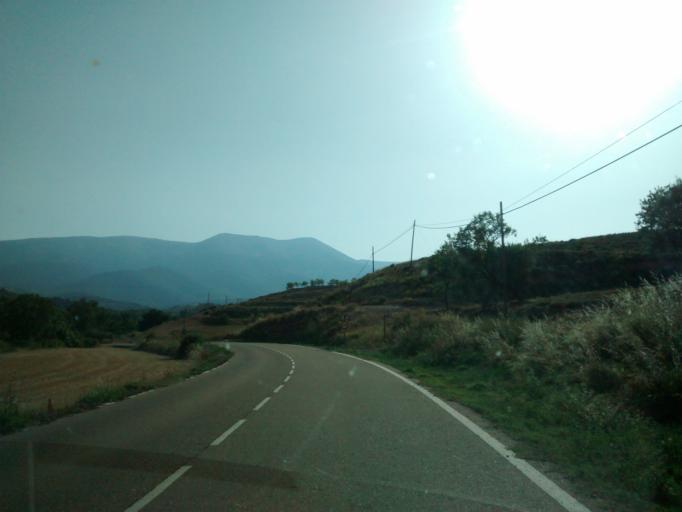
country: ES
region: Aragon
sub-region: Provincia de Zaragoza
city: Trasmoz
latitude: 41.8316
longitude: -1.7222
